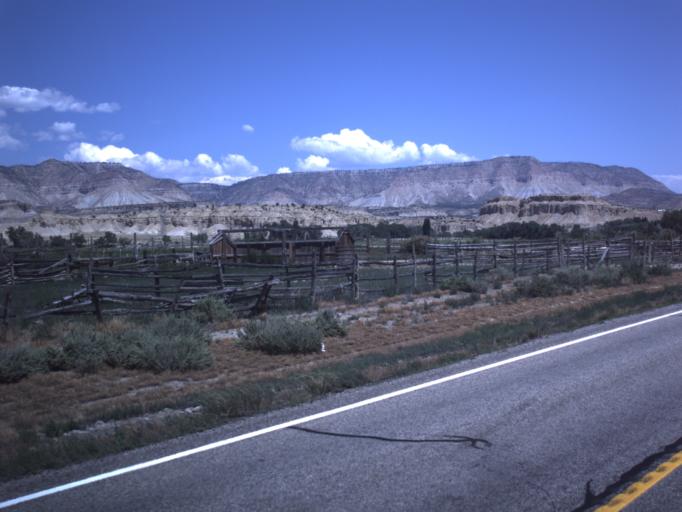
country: US
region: Utah
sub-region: Emery County
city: Ferron
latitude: 38.8699
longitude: -111.2952
